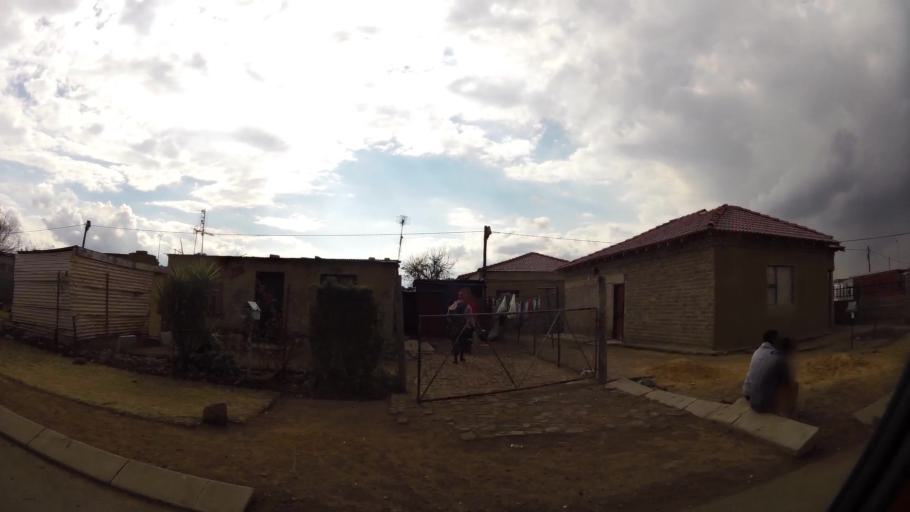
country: ZA
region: Gauteng
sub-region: Sedibeng District Municipality
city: Vanderbijlpark
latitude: -26.6884
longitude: 27.7829
